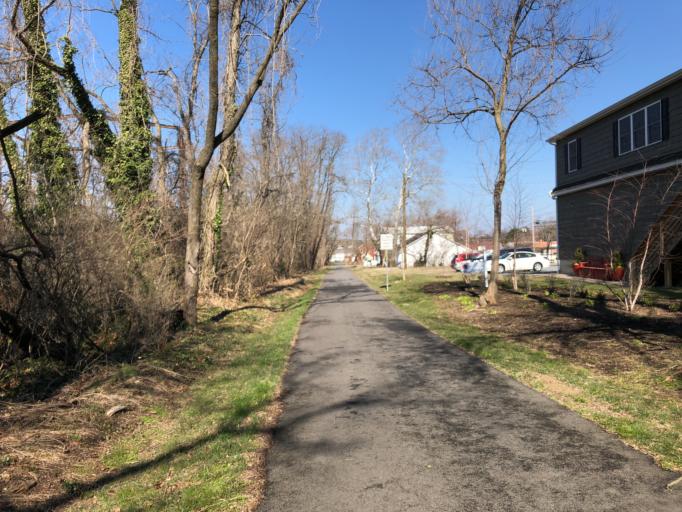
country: US
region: Maryland
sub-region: Kent County
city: Chestertown
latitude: 39.2147
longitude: -76.0757
